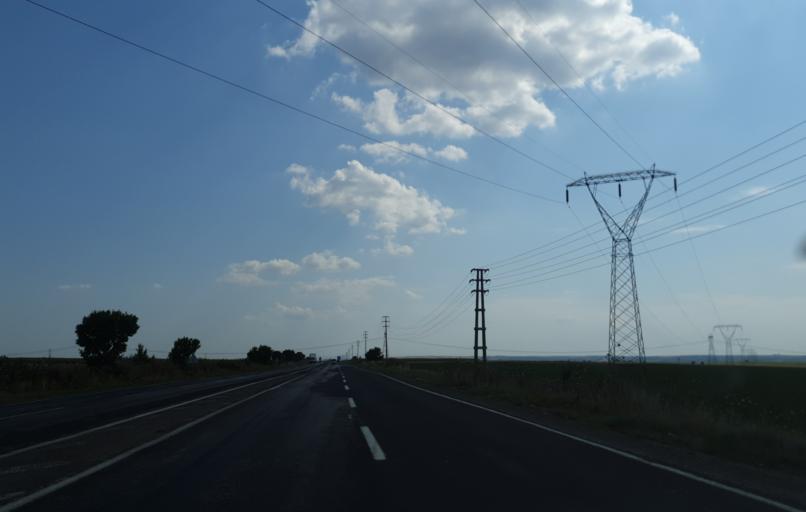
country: TR
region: Kirklareli
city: Buyukkaristiran
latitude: 41.2410
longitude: 27.5376
